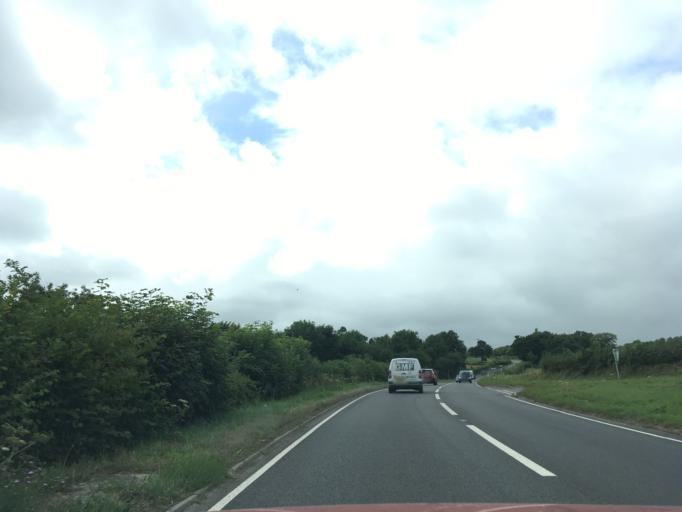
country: GB
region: Wales
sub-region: Carmarthenshire
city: Llanddarog
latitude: 51.8725
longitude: -4.1462
